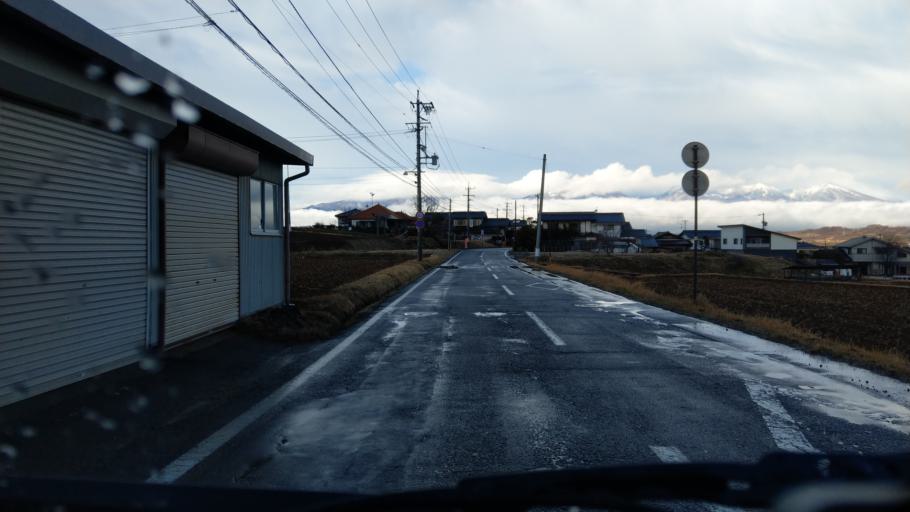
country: JP
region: Nagano
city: Kamimaruko
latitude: 36.2792
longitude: 138.3233
